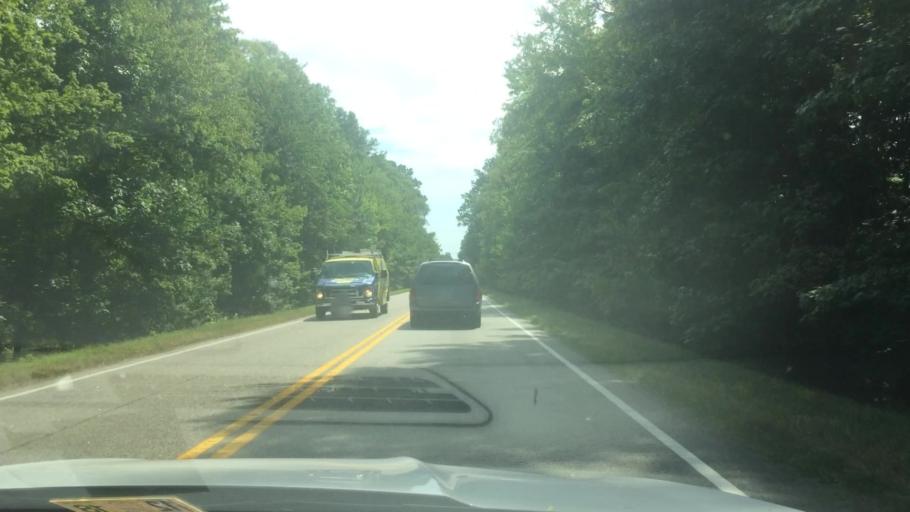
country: US
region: Virginia
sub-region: City of Poquoson
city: Poquoson
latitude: 37.1216
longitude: -76.4387
